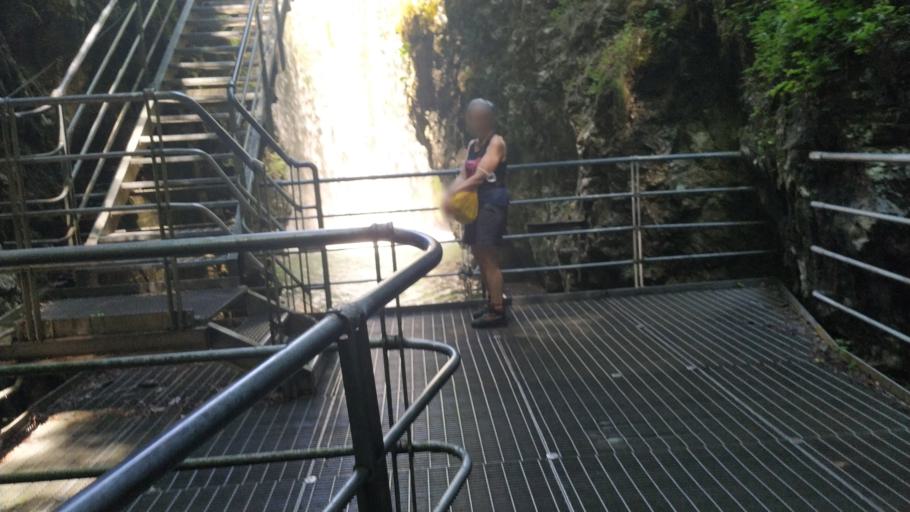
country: IT
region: Trentino-Alto Adige
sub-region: Provincia di Trento
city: Fondo
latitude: 46.4436
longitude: 11.1420
